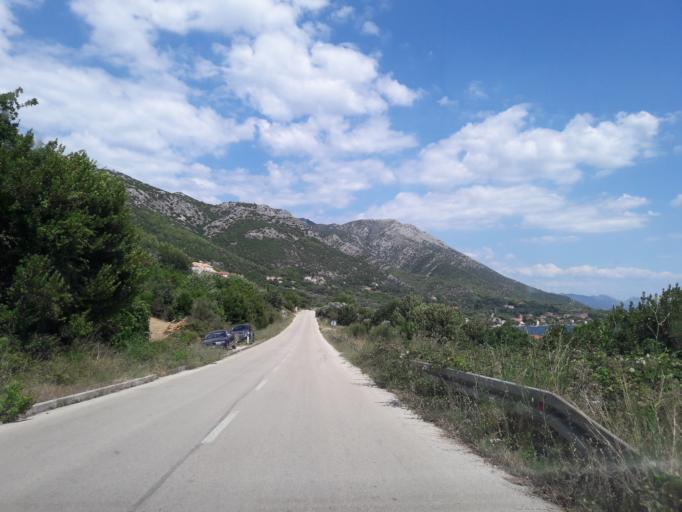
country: HR
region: Dubrovacko-Neretvanska
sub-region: Grad Korcula
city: Zrnovo
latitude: 42.9847
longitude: 17.0845
